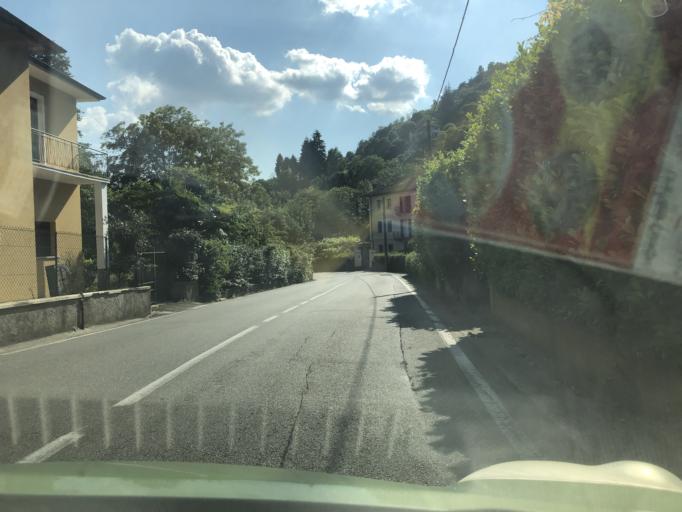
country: IT
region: Piedmont
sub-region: Provincia di Novara
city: Meina
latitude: 45.7769
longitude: 8.5378
